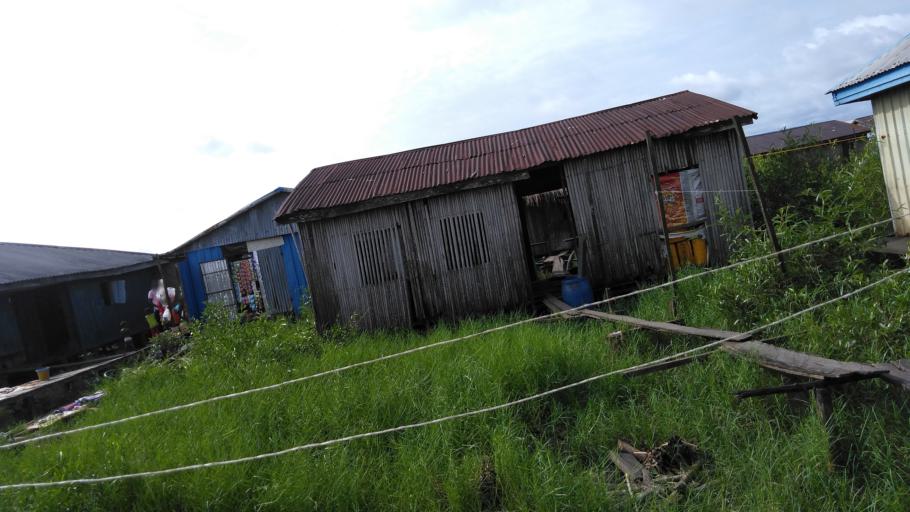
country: NG
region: Ondo
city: Igbekebo
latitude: 5.9261
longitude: 4.9619
